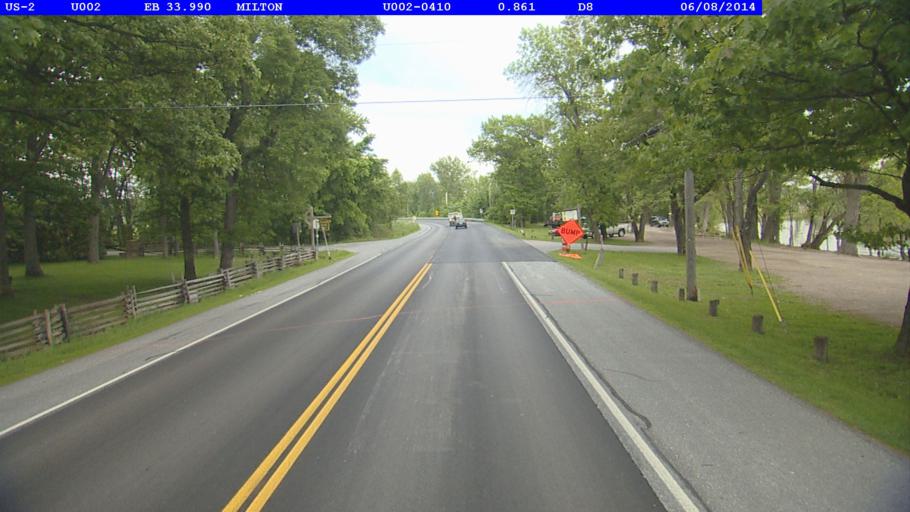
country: US
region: Vermont
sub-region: Chittenden County
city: Colchester
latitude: 44.6261
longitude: -73.2402
